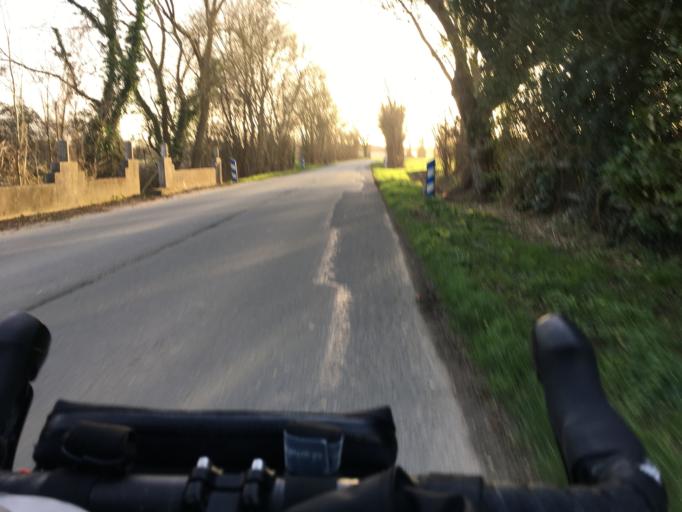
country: FR
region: Poitou-Charentes
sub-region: Departement de la Charente-Maritime
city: Courcon
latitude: 46.1674
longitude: -0.8526
